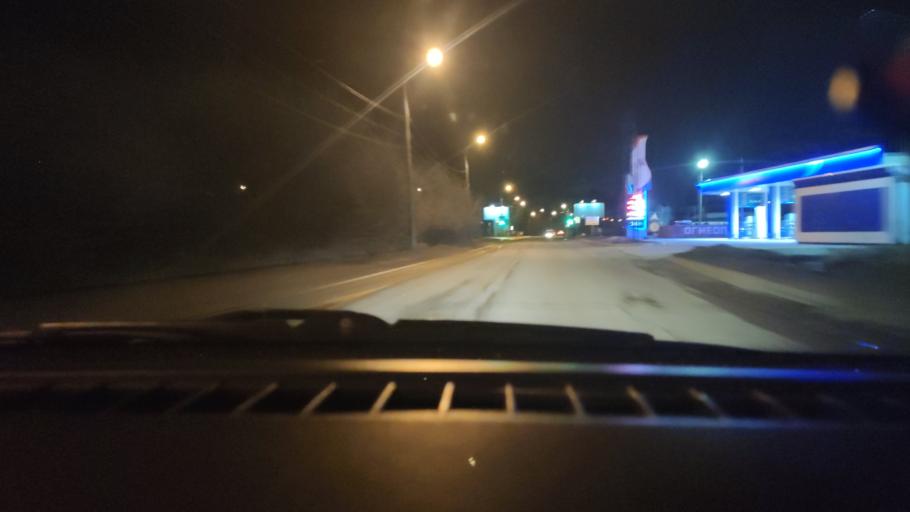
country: RU
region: Perm
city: Perm
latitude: 58.0725
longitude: 56.3485
